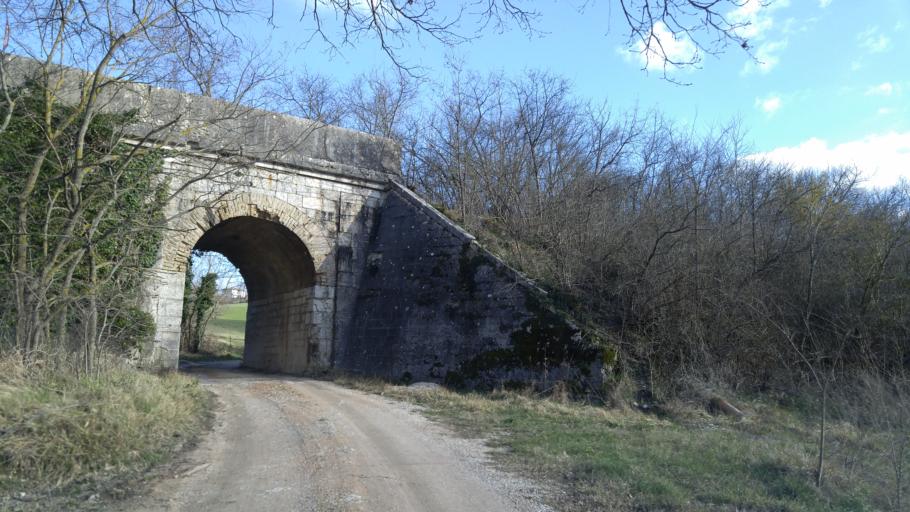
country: IT
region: The Marches
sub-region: Provincia di Pesaro e Urbino
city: Cagli
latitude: 43.5590
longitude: 12.6573
